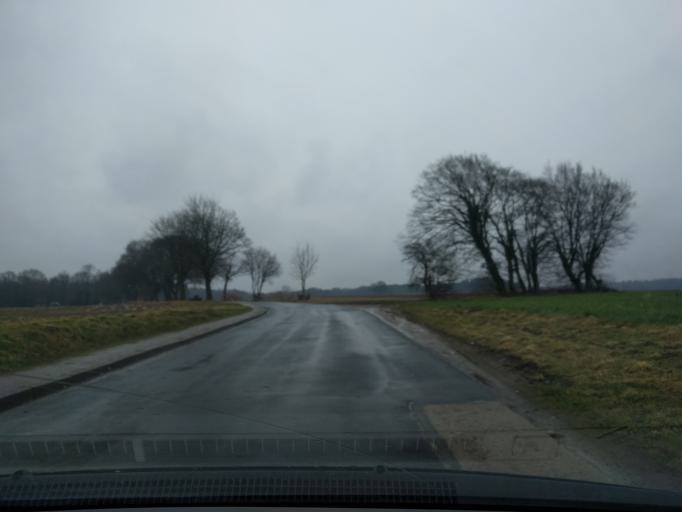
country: DE
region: Lower Saxony
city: Bendestorf
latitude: 53.3634
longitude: 9.9475
